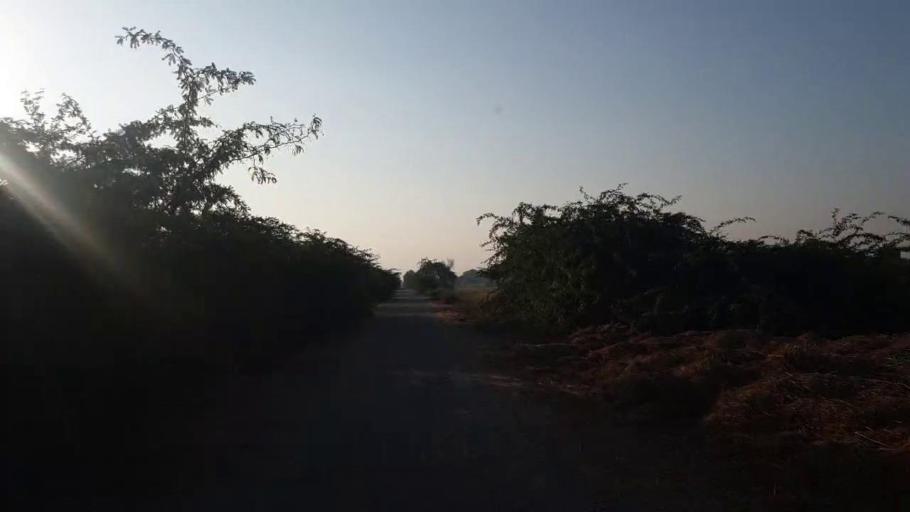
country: PK
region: Sindh
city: Badin
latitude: 24.6579
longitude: 68.7876
